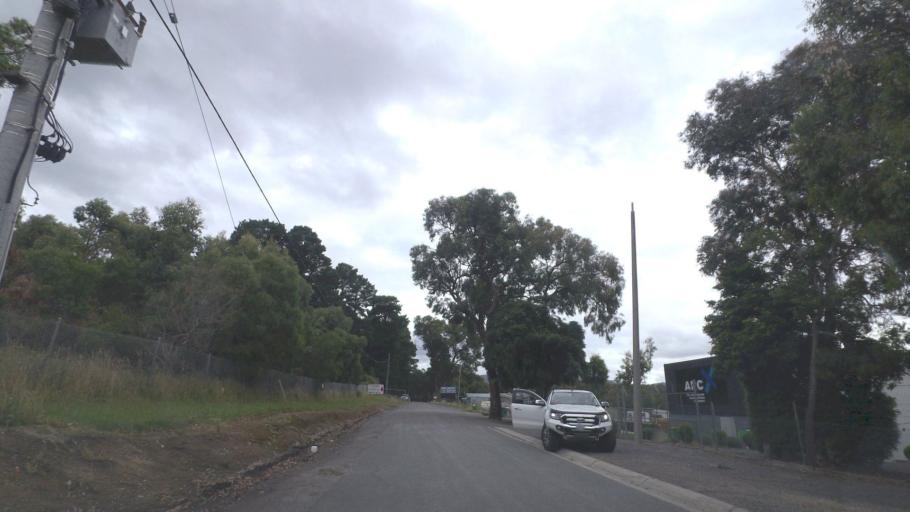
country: AU
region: Victoria
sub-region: Maroondah
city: Kilsyth South
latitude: -37.8220
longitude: 145.3261
